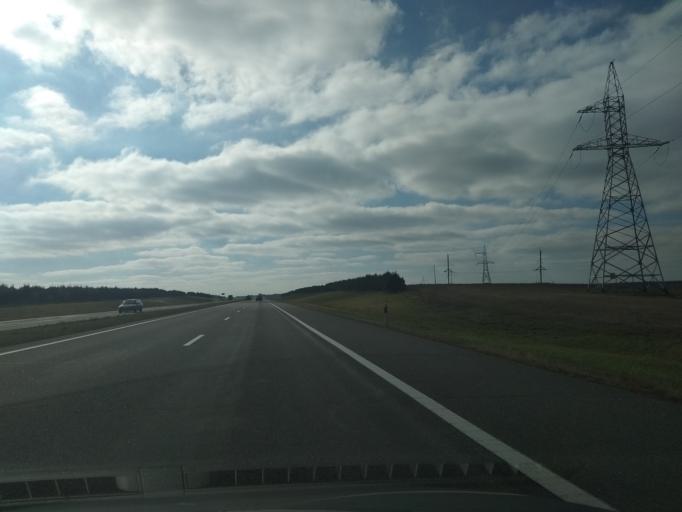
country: BY
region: Grodnenskaya
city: Mir
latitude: 53.4403
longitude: 26.5908
